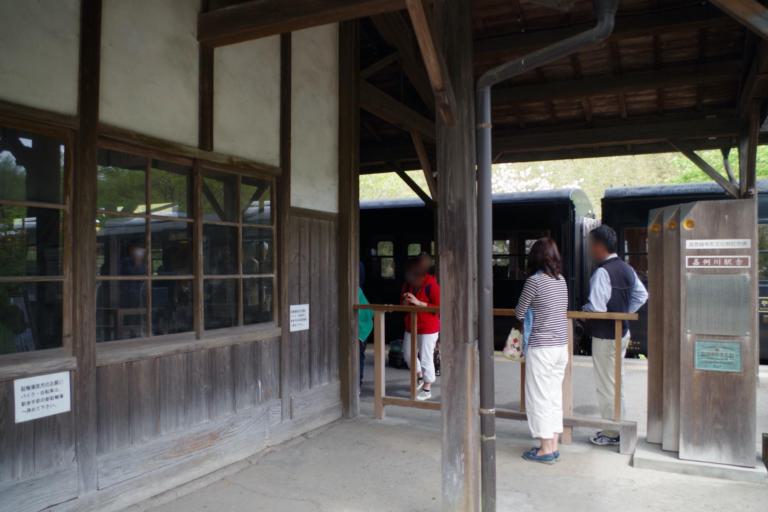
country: JP
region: Kagoshima
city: Kokubu-matsuki
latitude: 31.8267
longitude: 130.7229
